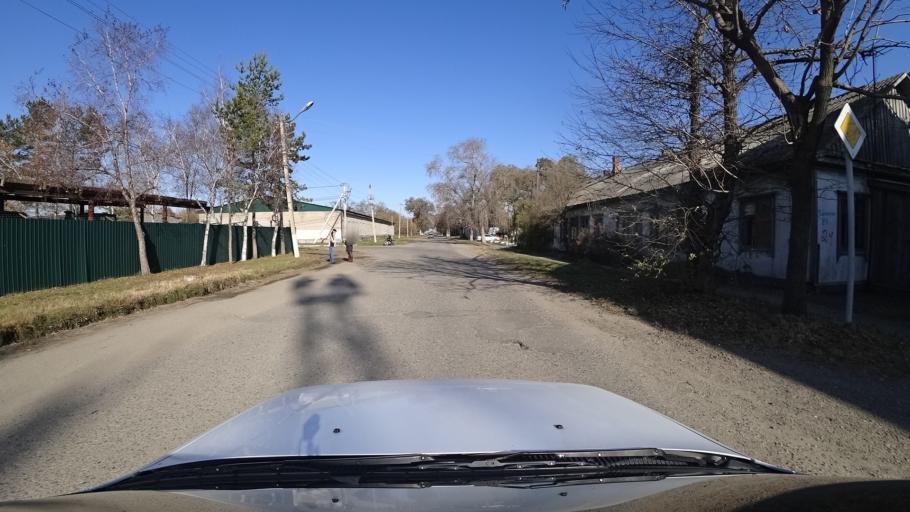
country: RU
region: Primorskiy
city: Dal'nerechensk
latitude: 45.9375
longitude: 133.7231
